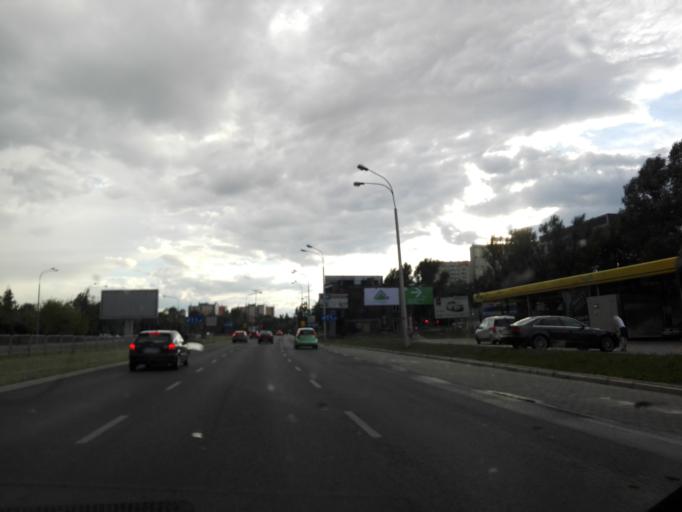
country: PL
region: Lublin Voivodeship
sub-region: Powiat lubelski
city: Lublin
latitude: 51.2534
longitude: 22.5551
